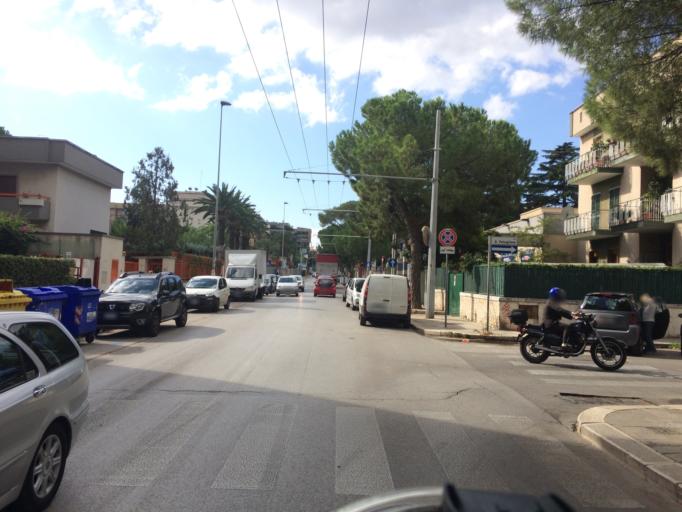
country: IT
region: Apulia
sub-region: Provincia di Bari
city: Bari
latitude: 41.0974
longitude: 16.8710
